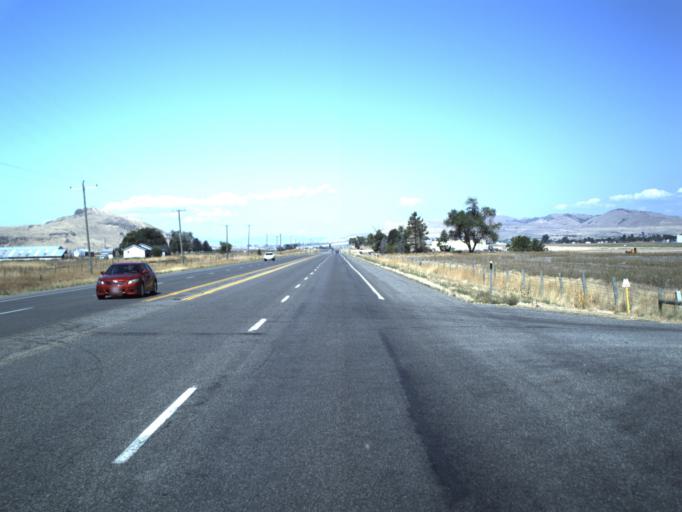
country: US
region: Utah
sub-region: Cache County
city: Lewiston
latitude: 41.9903
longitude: -111.8127
